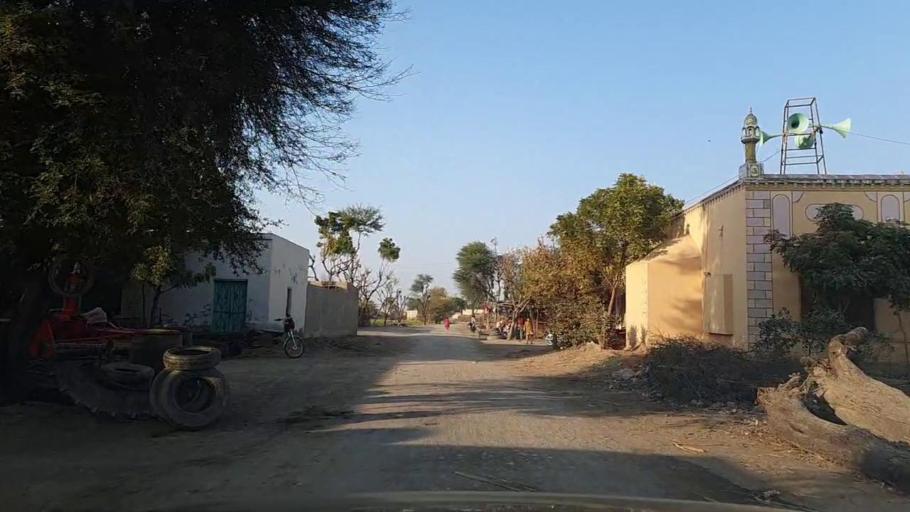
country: PK
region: Sindh
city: Tando Mittha Khan
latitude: 25.9449
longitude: 69.0763
